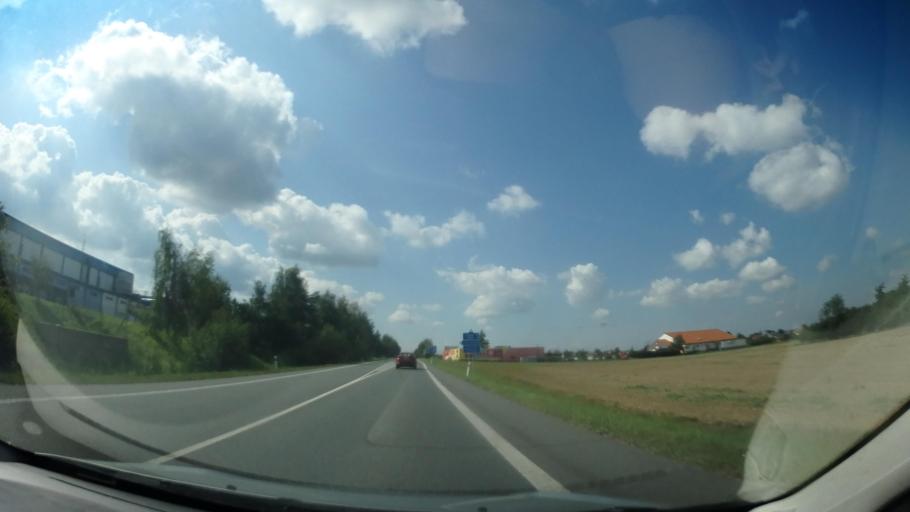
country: CZ
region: Central Bohemia
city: Kostelec nad Cernymi Lesy
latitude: 49.9858
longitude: 14.8626
